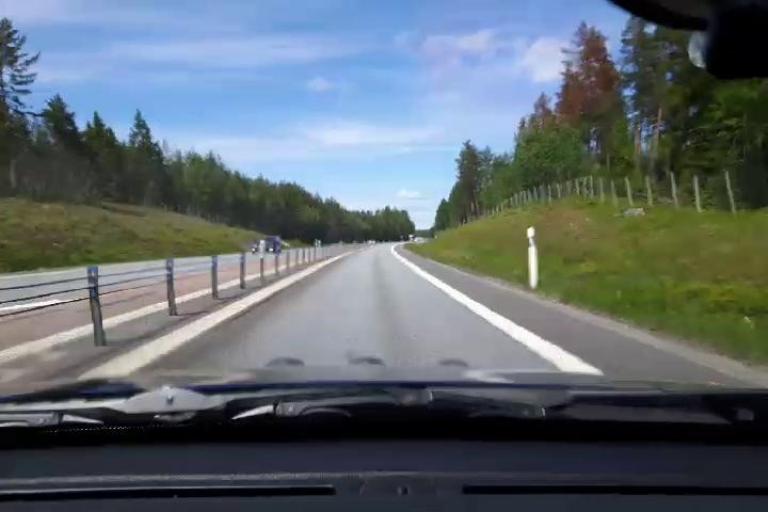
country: SE
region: Gaevleborg
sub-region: Gavle Kommun
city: Gavle
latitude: 60.7320
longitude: 17.0754
